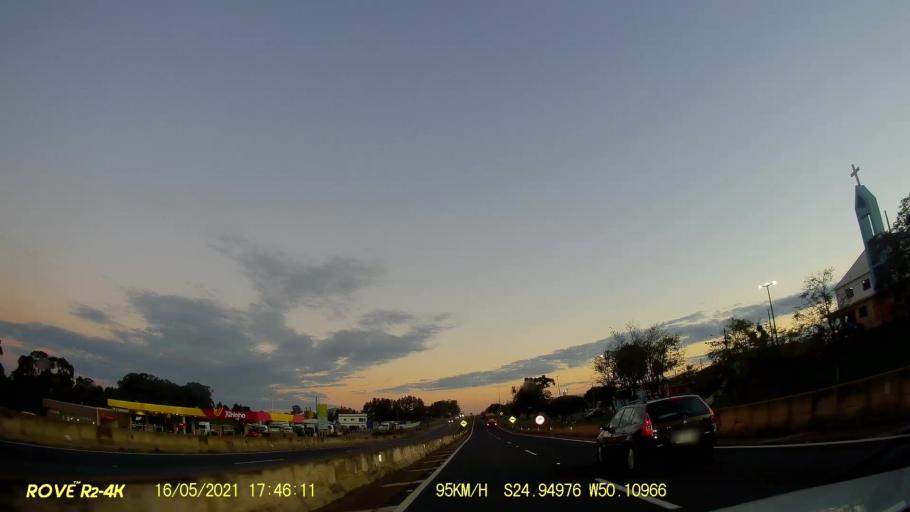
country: BR
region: Parana
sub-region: Carambei
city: Carambei
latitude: -24.9498
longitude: -50.1097
